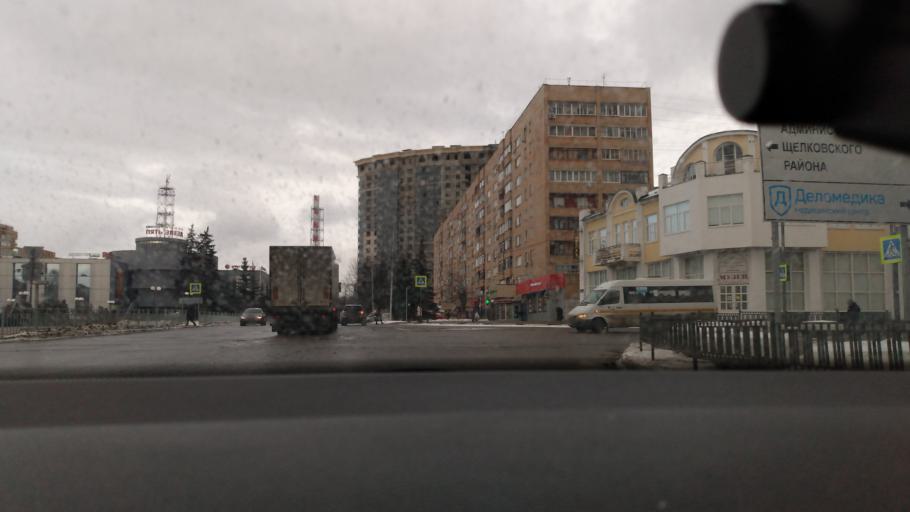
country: RU
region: Moskovskaya
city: Shchelkovo
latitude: 55.9198
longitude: 37.9921
